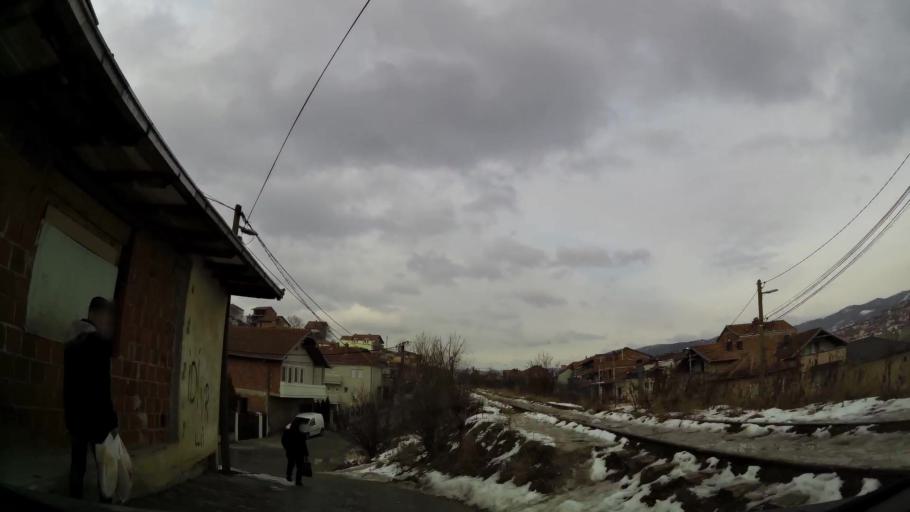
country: XK
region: Pristina
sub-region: Komuna e Prishtines
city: Pristina
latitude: 42.6779
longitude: 21.1704
